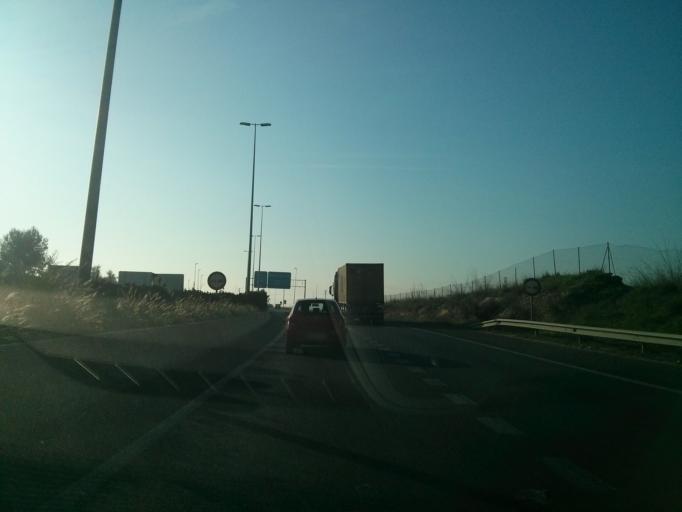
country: ES
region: Valencia
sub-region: Provincia de Valencia
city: Paterna
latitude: 39.4967
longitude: -0.4283
